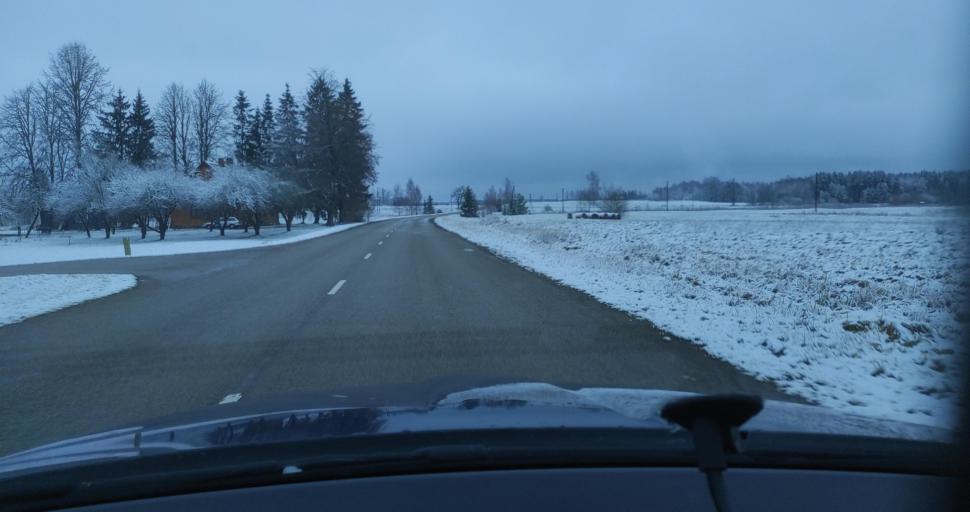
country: LV
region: Skrunda
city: Skrunda
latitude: 56.8766
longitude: 22.2403
